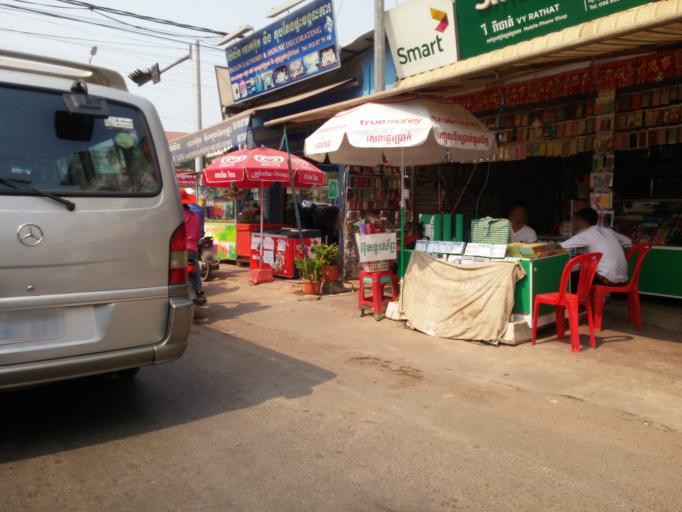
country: KH
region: Siem Reap
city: Siem Reap
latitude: 13.3634
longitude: 103.8623
